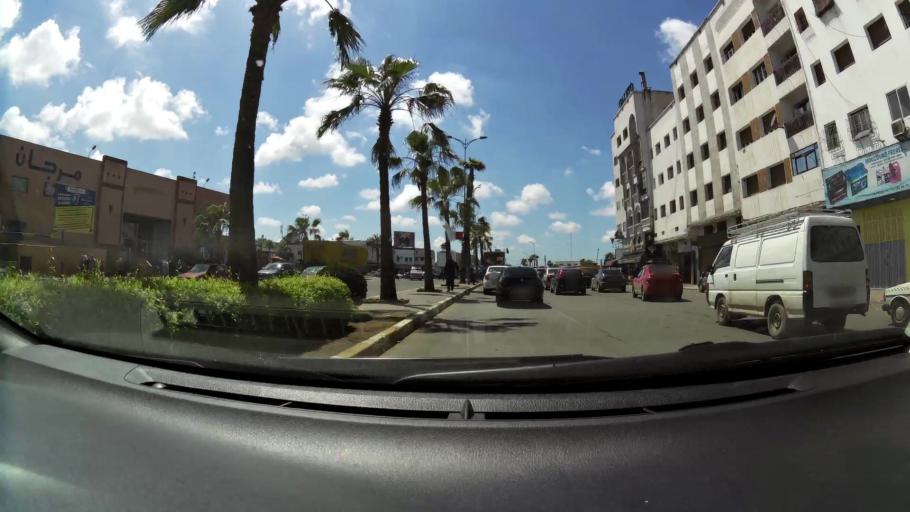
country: MA
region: Grand Casablanca
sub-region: Casablanca
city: Casablanca
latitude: 33.5629
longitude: -7.5939
